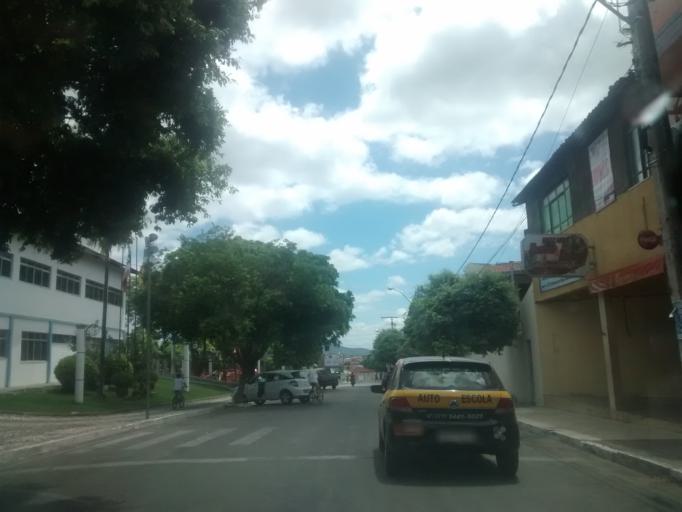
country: BR
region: Bahia
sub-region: Brumado
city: Brumado
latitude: -14.2042
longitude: -41.6699
